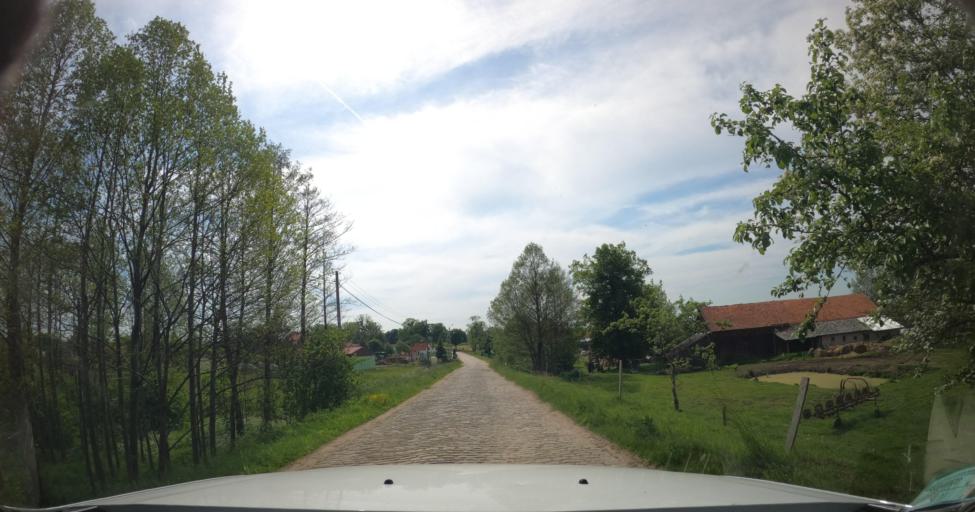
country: PL
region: Warmian-Masurian Voivodeship
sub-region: Powiat lidzbarski
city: Lubomino
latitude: 54.1022
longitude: 20.3266
